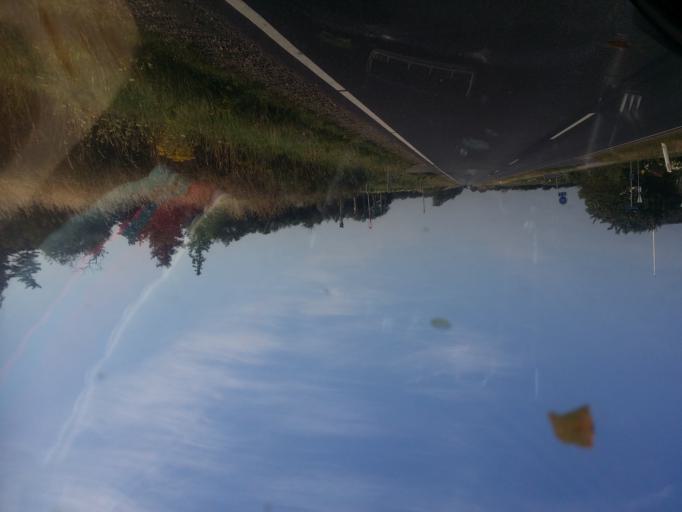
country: DK
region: South Denmark
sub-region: Tonder Kommune
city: Sherrebek
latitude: 55.2234
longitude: 8.7251
